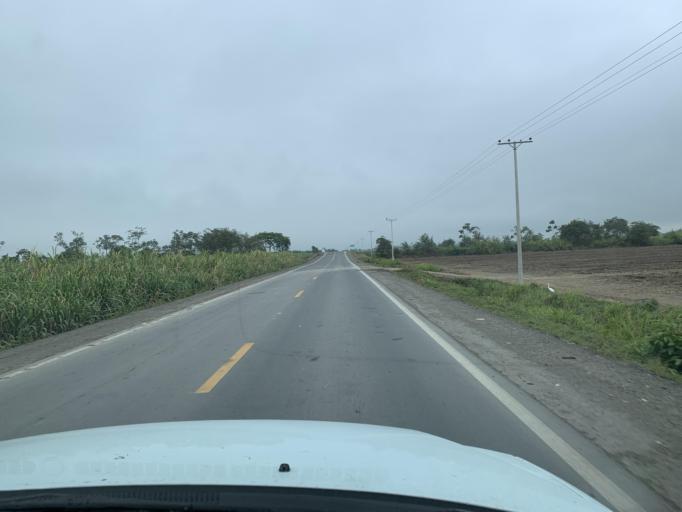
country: EC
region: Guayas
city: Coronel Marcelino Mariduena
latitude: -2.3108
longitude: -79.5110
